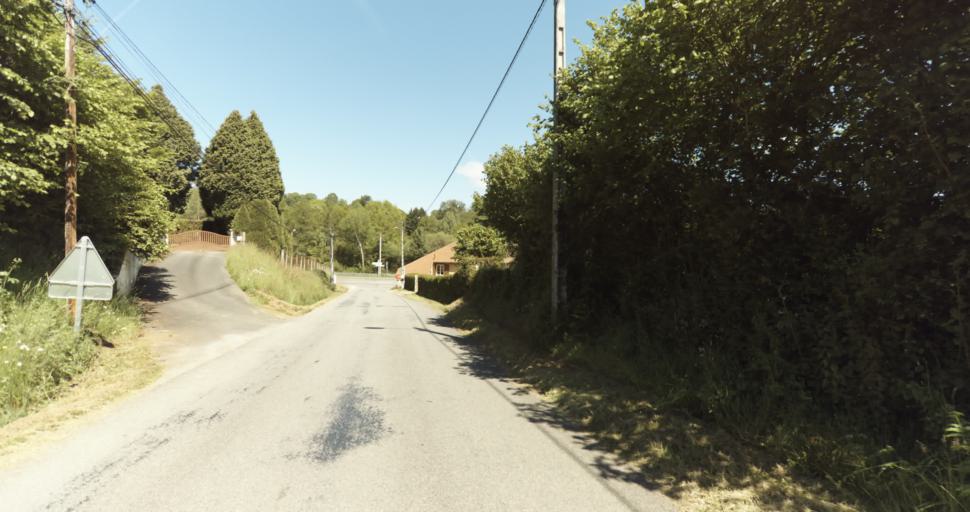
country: FR
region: Limousin
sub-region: Departement de la Haute-Vienne
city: Le Vigen
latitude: 45.7386
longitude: 1.2821
